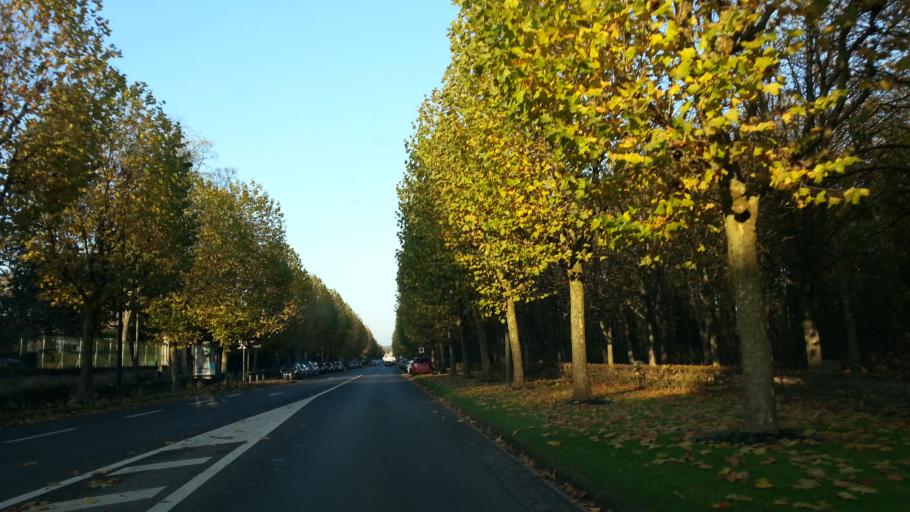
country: FR
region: Picardie
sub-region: Departement de l'Oise
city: Chantilly
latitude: 49.1874
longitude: 2.4615
